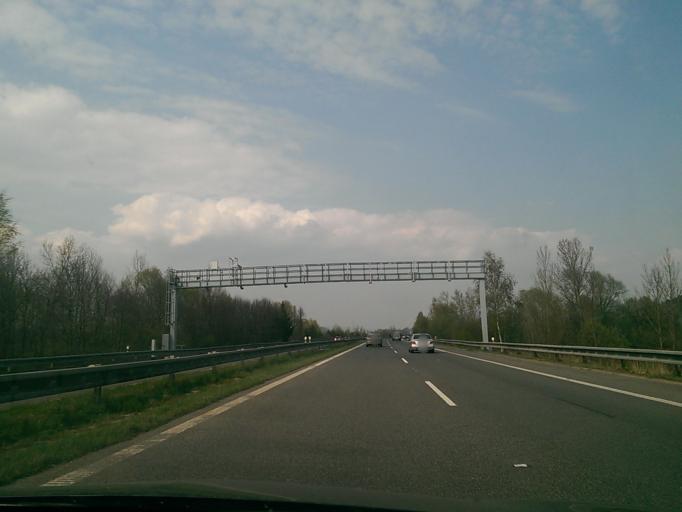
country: CZ
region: Central Bohemia
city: Mnichovo Hradiste
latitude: 50.4986
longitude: 14.9756
